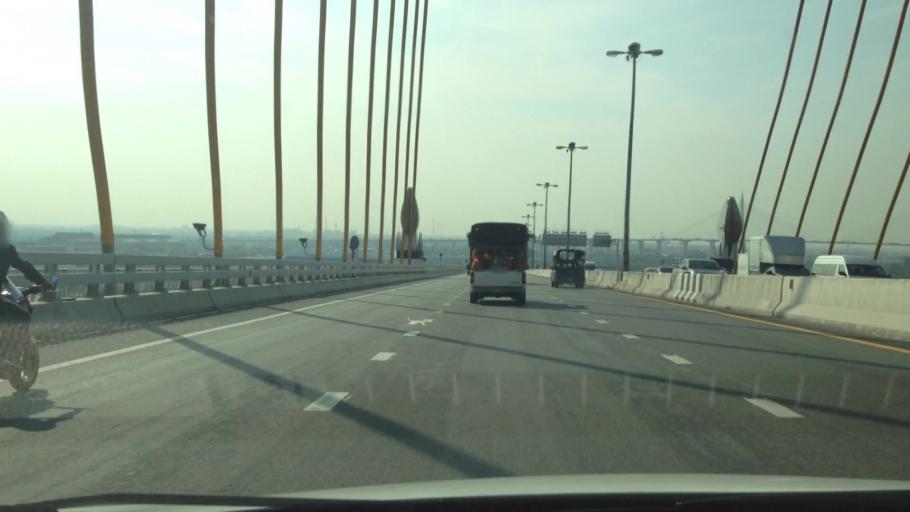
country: TH
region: Samut Prakan
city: Phra Pradaeng
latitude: 13.6585
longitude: 100.5401
